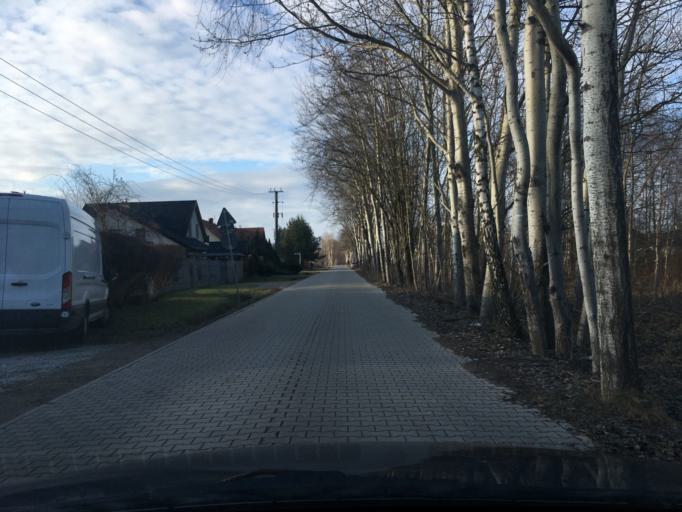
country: PL
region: Masovian Voivodeship
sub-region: Powiat piaseczynski
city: Lesznowola
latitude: 52.0271
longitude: 20.9400
